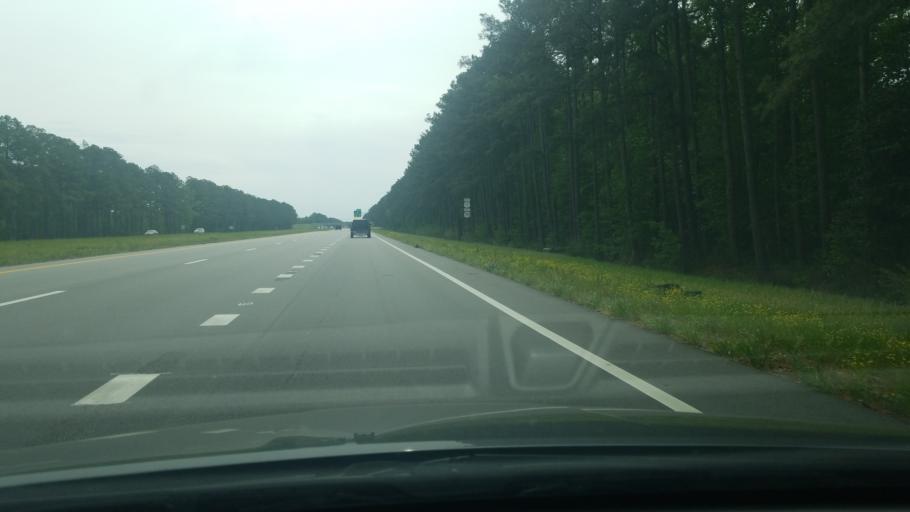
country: US
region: North Carolina
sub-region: Craven County
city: River Bend
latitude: 35.1303
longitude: -77.1455
